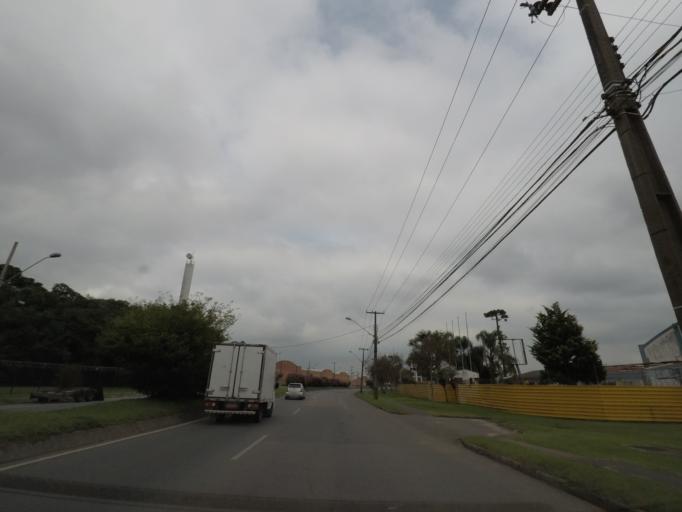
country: BR
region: Parana
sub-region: Curitiba
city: Curitiba
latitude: -25.5073
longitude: -49.3294
